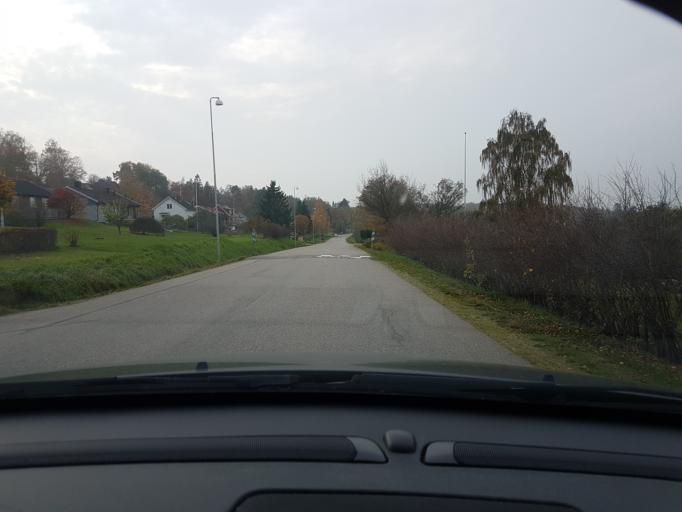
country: SE
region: Vaestra Goetaland
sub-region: Ale Kommun
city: Alvangen
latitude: 57.9471
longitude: 12.1036
